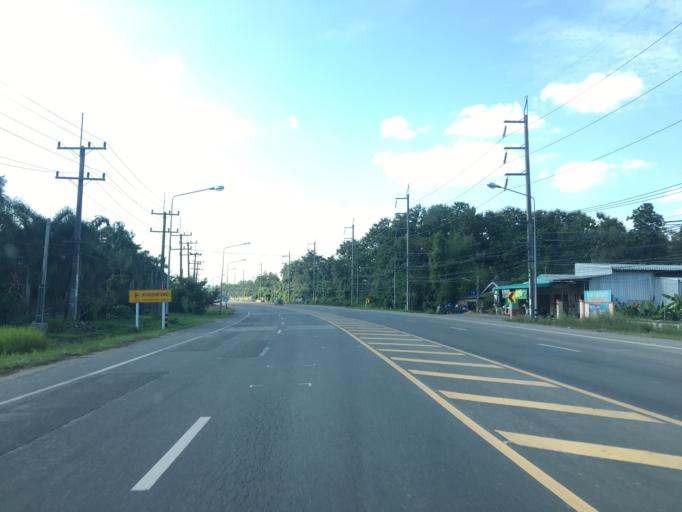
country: TH
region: Phayao
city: Chun
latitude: 19.3337
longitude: 100.1375
